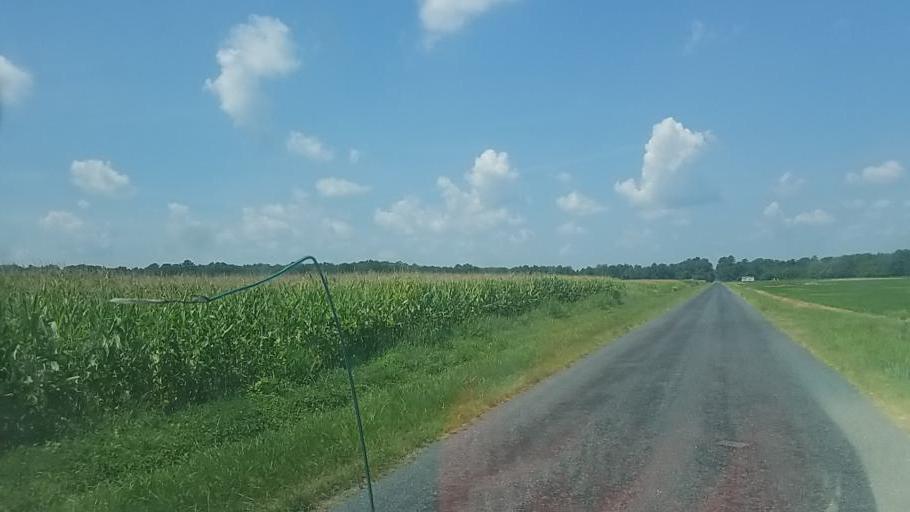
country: US
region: Maryland
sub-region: Worcester County
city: Berlin
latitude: 38.2977
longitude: -75.2771
